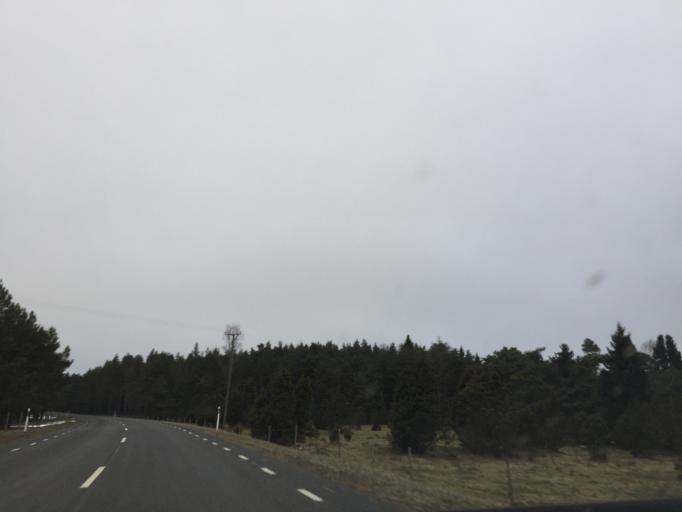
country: EE
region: Saare
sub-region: Kuressaare linn
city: Kuressaare
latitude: 58.5440
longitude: 22.3375
